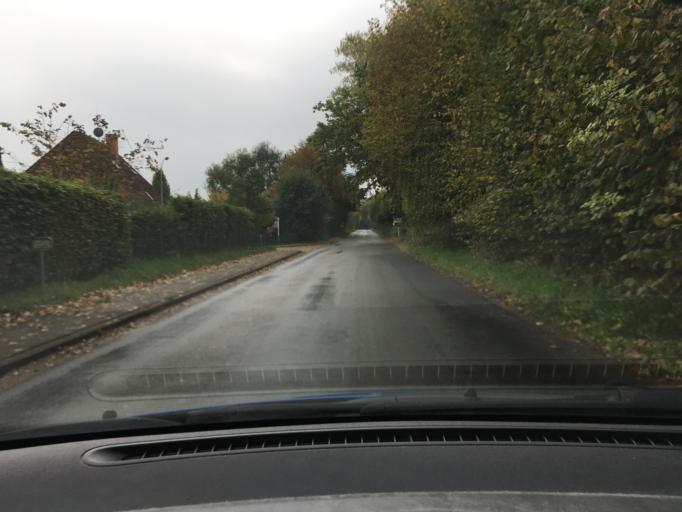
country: DE
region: Schleswig-Holstein
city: Bosau
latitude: 54.1024
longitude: 10.4301
